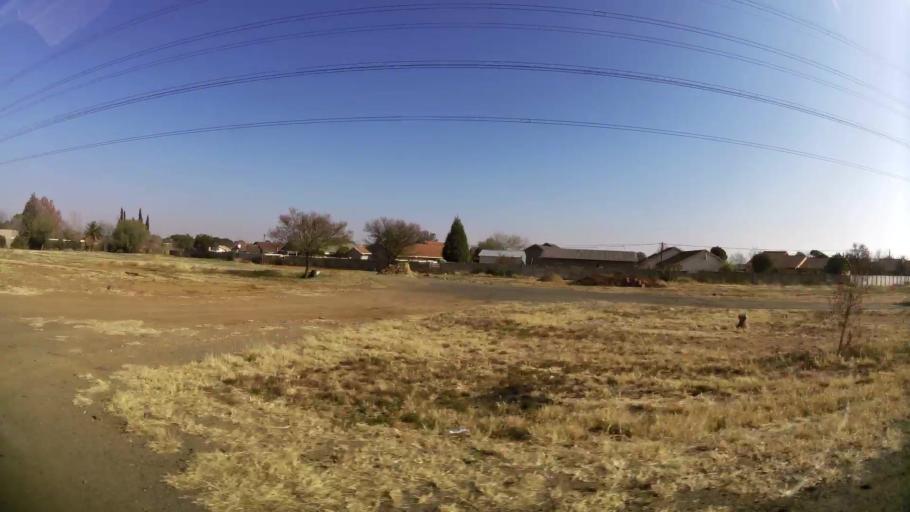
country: ZA
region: Orange Free State
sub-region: Mangaung Metropolitan Municipality
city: Bloemfontein
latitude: -29.1779
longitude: 26.1911
